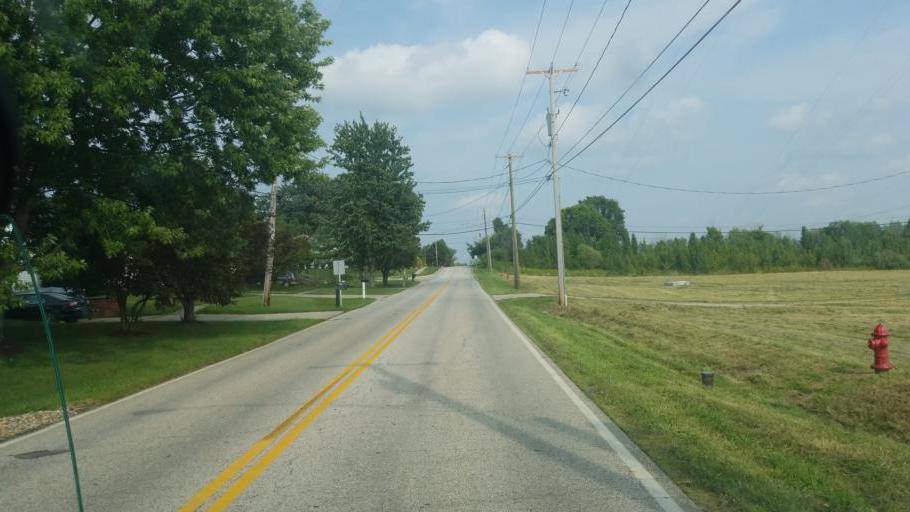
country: US
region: Ohio
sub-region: Medina County
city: Medina
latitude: 41.1424
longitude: -81.8957
